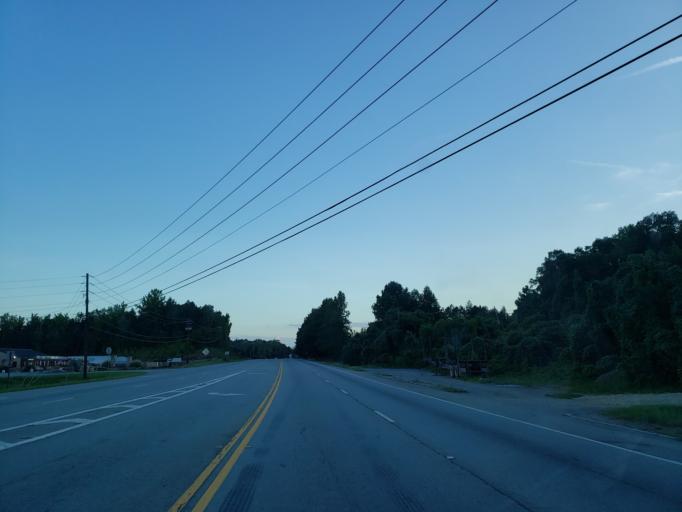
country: US
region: Georgia
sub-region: Floyd County
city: Lindale
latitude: 34.1935
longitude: -85.2012
